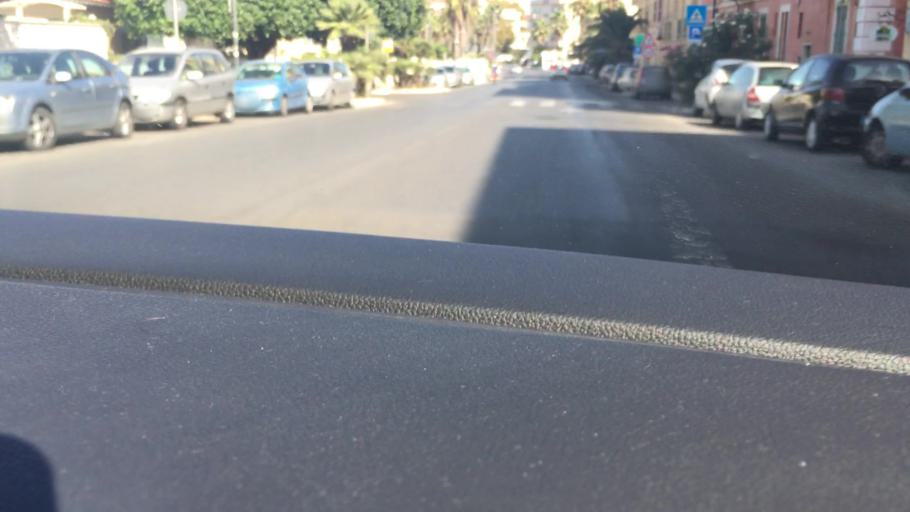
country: IT
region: Latium
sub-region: Citta metropolitana di Roma Capitale
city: Anzio
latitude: 41.4459
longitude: 12.6229
